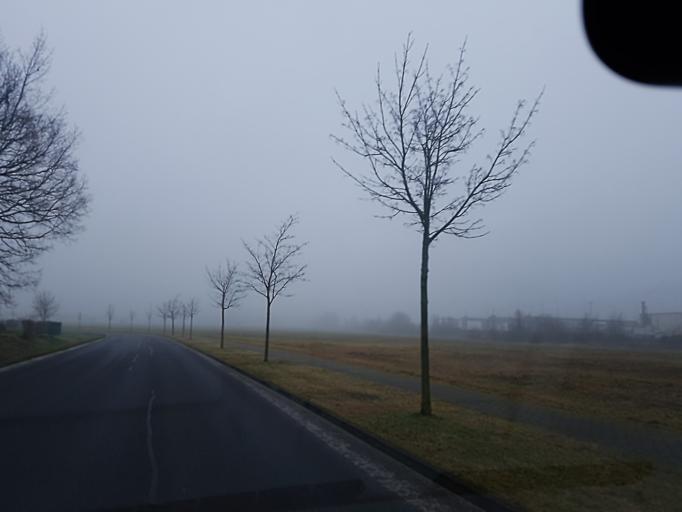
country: DE
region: Brandenburg
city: Finsterwalde
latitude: 51.6315
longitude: 13.7332
